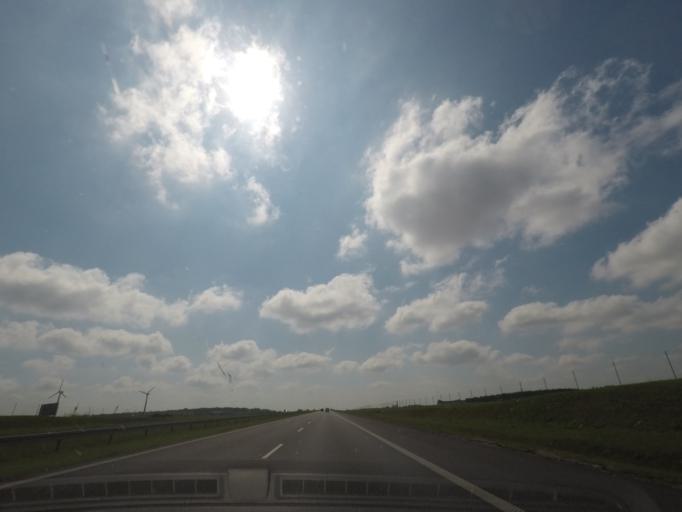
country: PL
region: Kujawsko-Pomorskie
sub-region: Powiat wloclawski
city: Brzesc Kujawski
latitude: 52.6439
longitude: 18.9447
